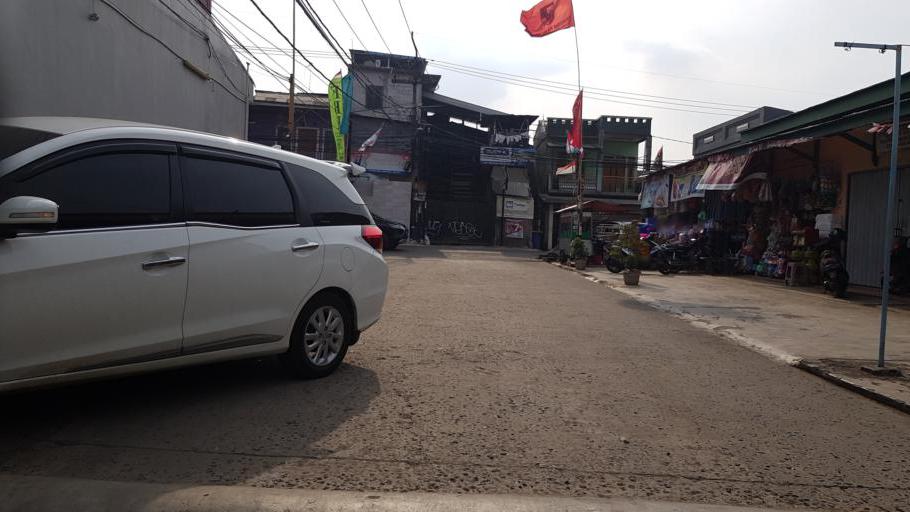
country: ID
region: West Java
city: Pamulang
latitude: -6.3280
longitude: 106.7971
